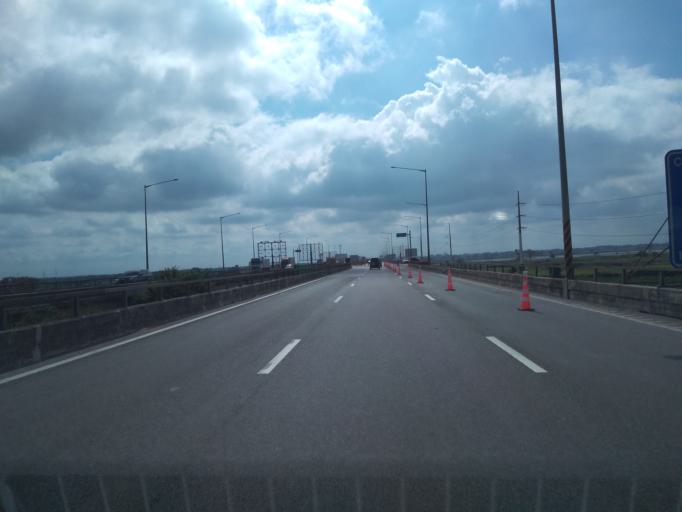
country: PH
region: Central Luzon
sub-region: Province of Pampanga
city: Balucuc
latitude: 14.9346
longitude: 120.7939
